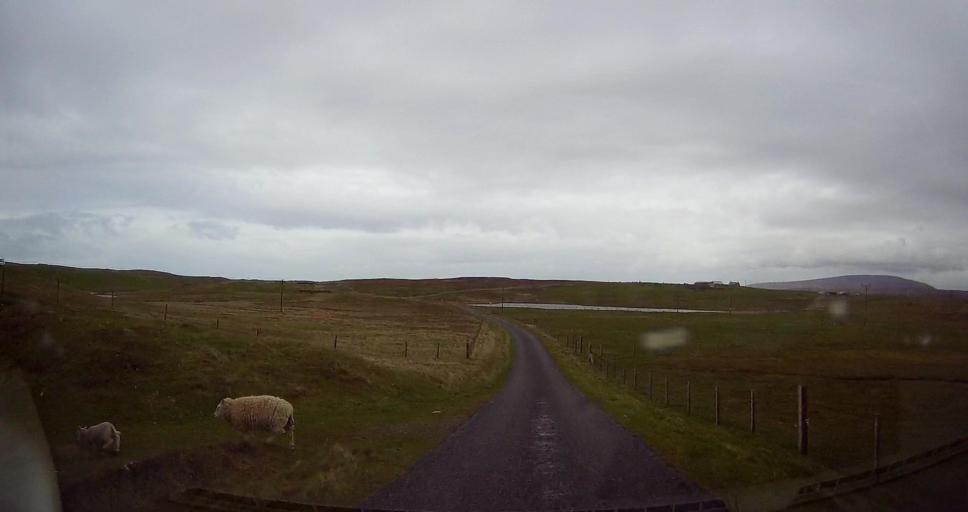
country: GB
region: Scotland
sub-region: Shetland Islands
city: Lerwick
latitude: 60.4810
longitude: -1.6094
